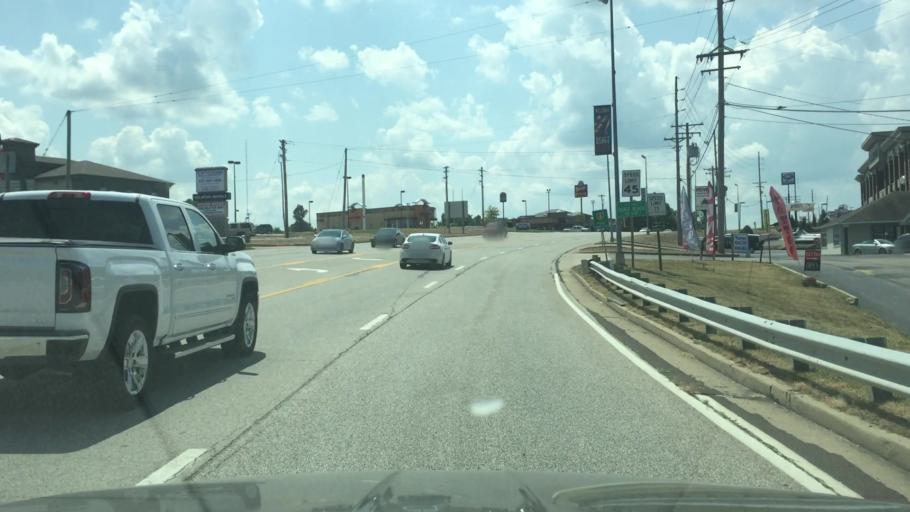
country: US
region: Missouri
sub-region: Miller County
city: Lake Ozark
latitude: 38.1710
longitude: -92.6124
